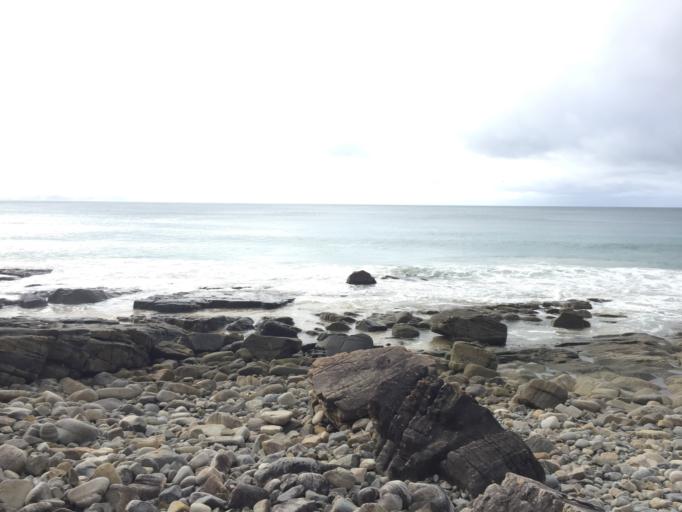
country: AU
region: Queensland
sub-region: Sunshine Coast
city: Noosa Heads
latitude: -26.3796
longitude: 153.1027
